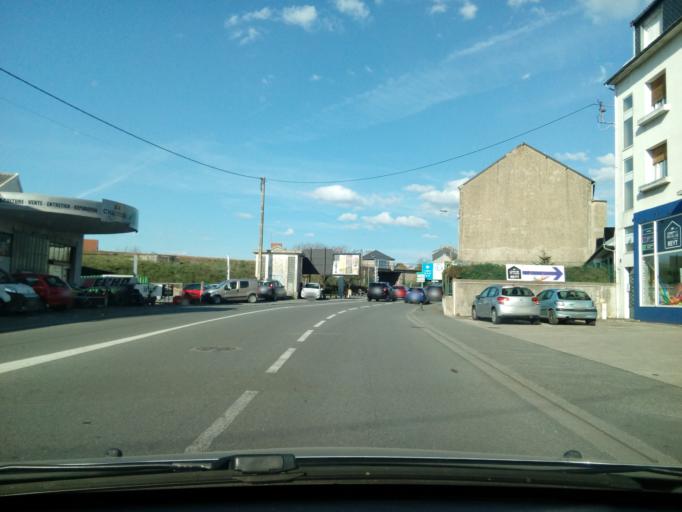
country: FR
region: Limousin
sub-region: Departement de la Creuse
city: Gueret
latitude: 46.1744
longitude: 1.8729
